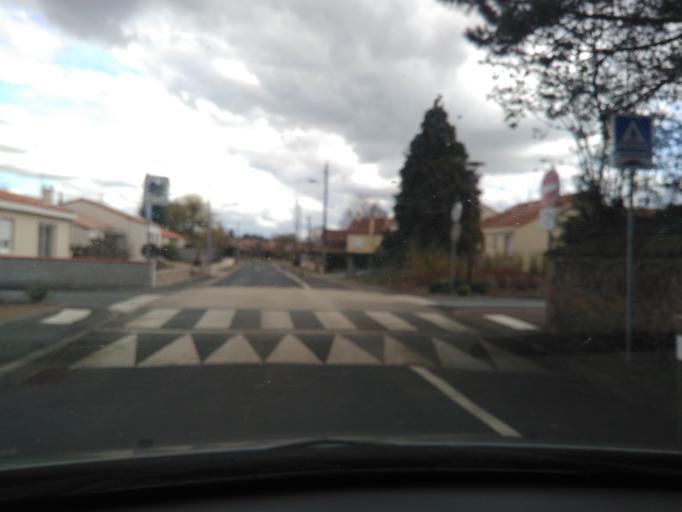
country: FR
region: Pays de la Loire
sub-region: Departement de la Vendee
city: Saint-Martin-des-Noyers
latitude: 46.7225
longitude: -1.1784
